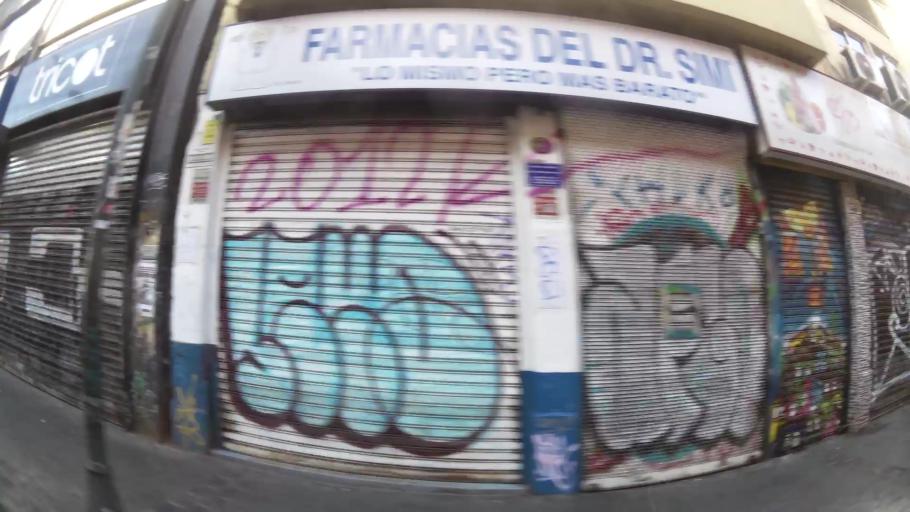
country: CL
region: Valparaiso
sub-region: Provincia de Valparaiso
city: Valparaiso
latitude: -33.0428
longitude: -71.6246
